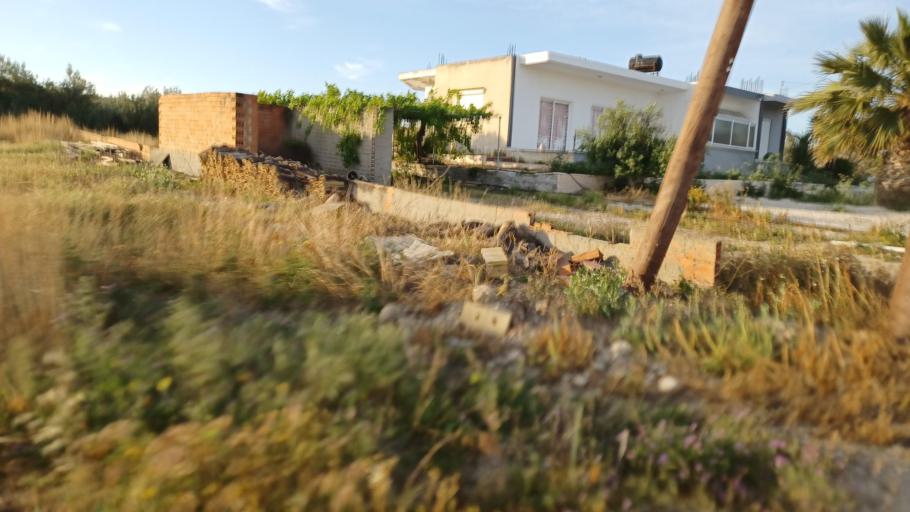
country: CY
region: Lefkosia
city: Akaki
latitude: 35.1701
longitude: 33.1509
